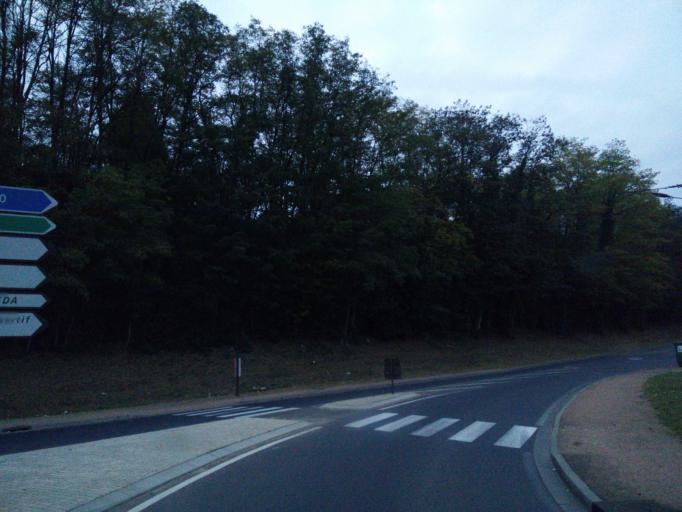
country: FR
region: Aquitaine
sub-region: Departement de la Dordogne
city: Sarlat-la-Caneda
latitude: 44.8770
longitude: 1.2174
